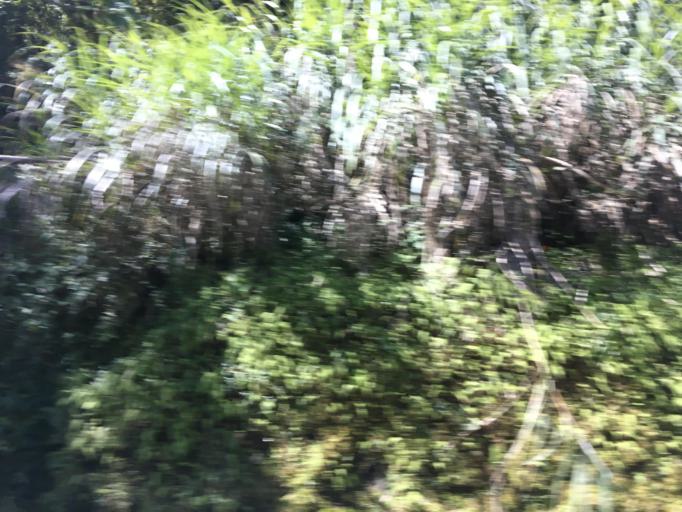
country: TW
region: Taiwan
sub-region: Yilan
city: Yilan
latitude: 24.5246
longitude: 121.5169
